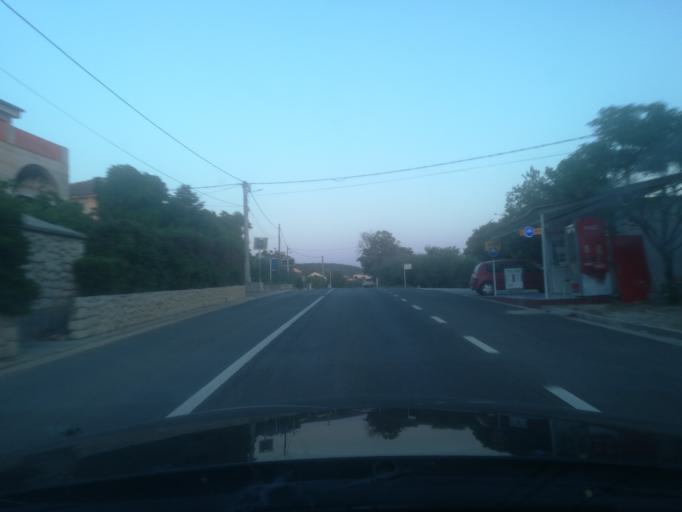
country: HR
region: Primorsko-Goranska
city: Banjol
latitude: 44.7319
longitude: 14.8116
